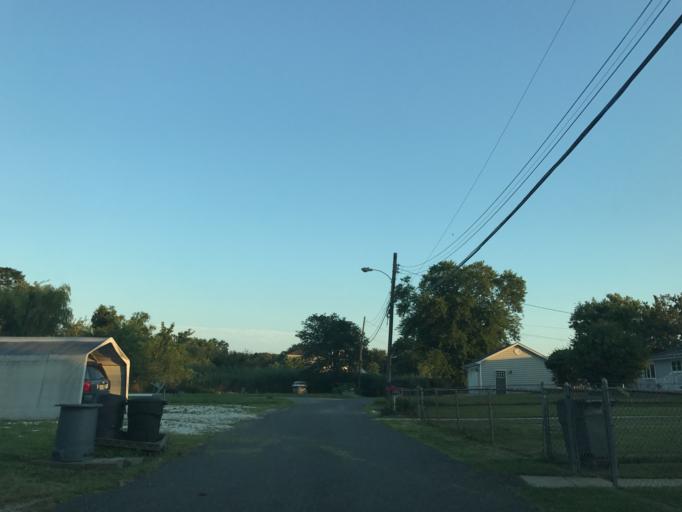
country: US
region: Maryland
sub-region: Baltimore County
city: Edgemere
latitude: 39.2746
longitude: -76.4377
